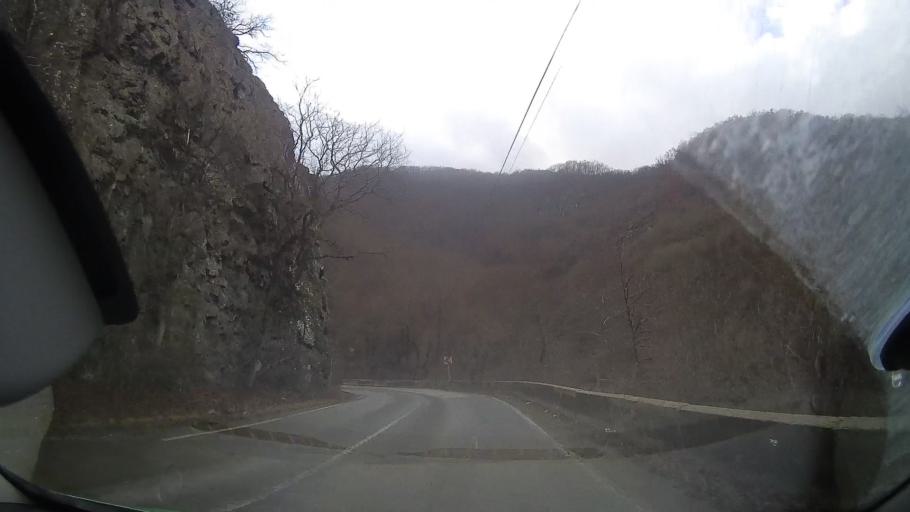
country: RO
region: Cluj
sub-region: Comuna Moldovenesti
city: Moldovenesti
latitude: 46.5038
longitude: 23.6231
